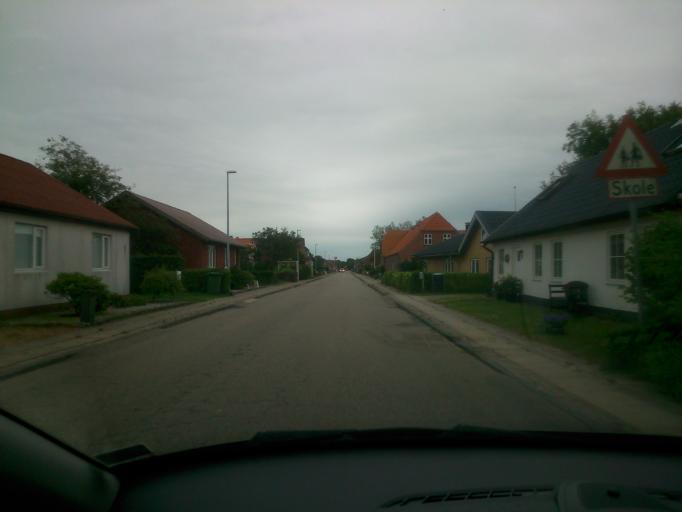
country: DK
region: Central Jutland
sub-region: Ringkobing-Skjern Kommune
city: Skjern
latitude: 55.9657
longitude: 8.3702
